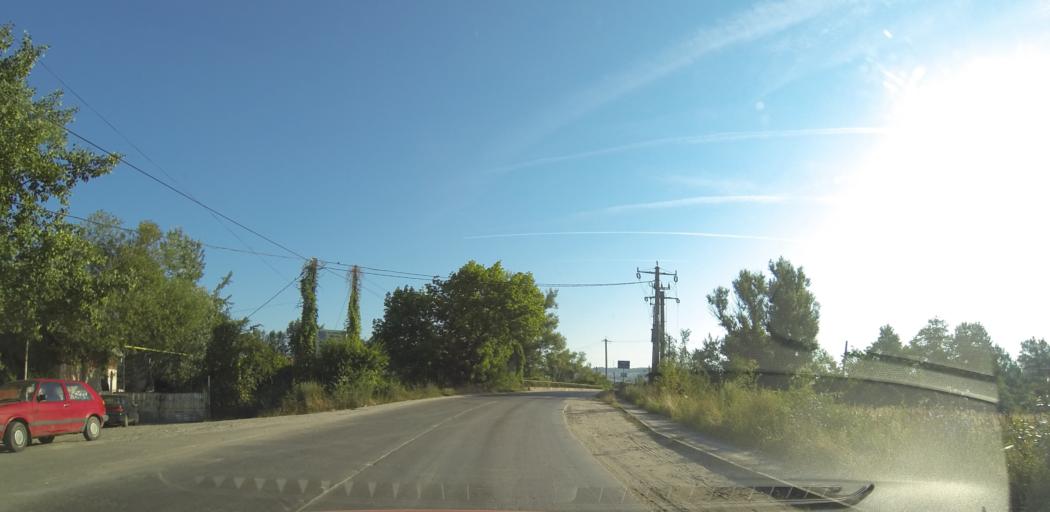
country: RO
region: Valcea
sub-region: Comuna Balcesti
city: Balcesti
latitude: 44.6284
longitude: 23.9411
